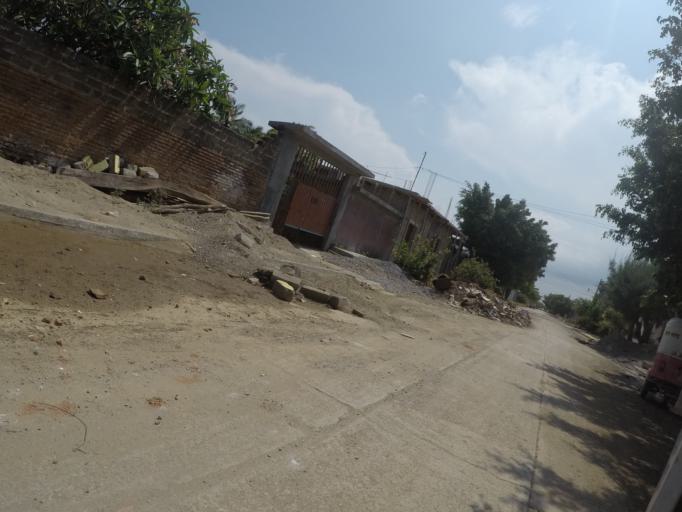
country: MX
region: Oaxaca
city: Union Hidalgo
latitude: 16.4745
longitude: -94.8320
